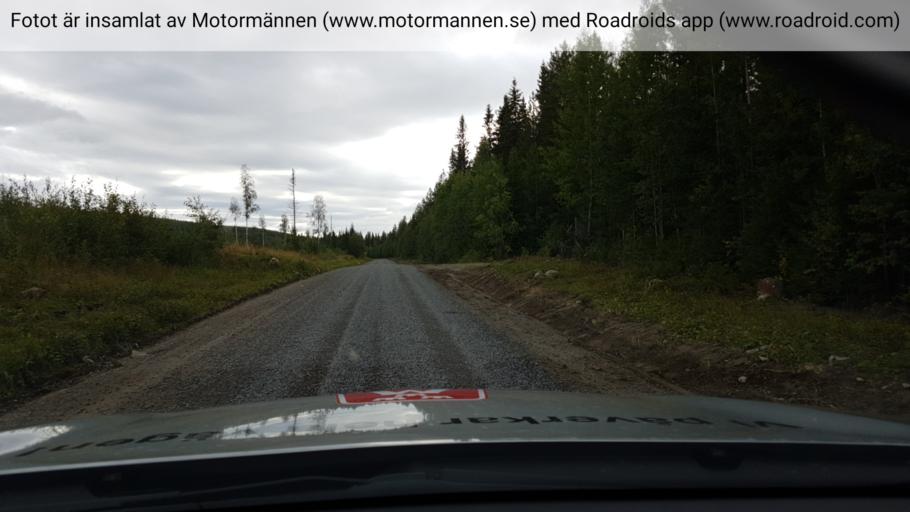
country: SE
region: Jaemtland
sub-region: Ragunda Kommun
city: Hammarstrand
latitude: 62.8788
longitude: 16.0598
